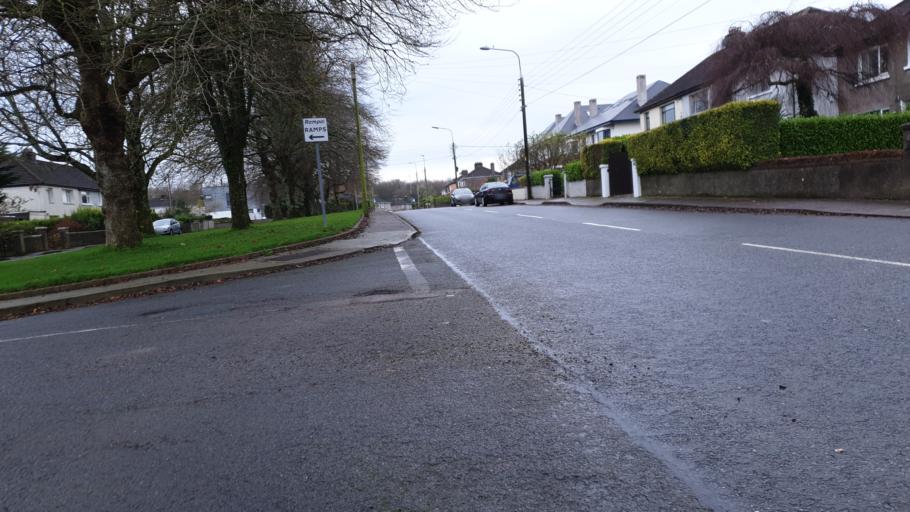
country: IE
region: Munster
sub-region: County Cork
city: Cork
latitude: 51.8914
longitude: -8.4239
